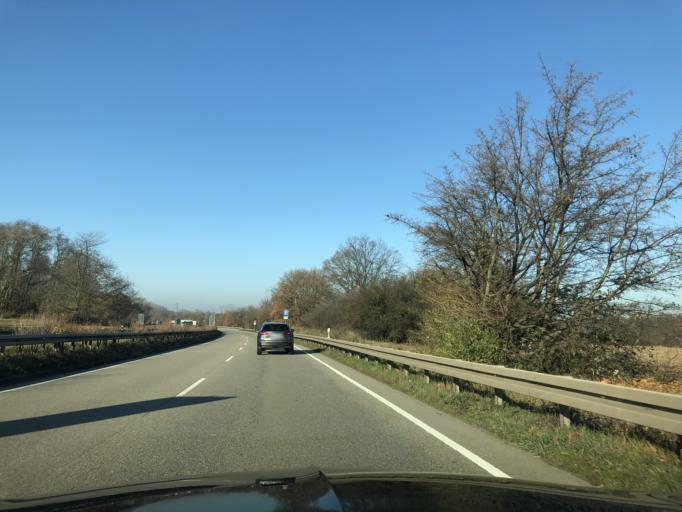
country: DE
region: Baden-Wuerttemberg
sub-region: Karlsruhe Region
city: Muggensturm
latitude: 48.8570
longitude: 8.2625
